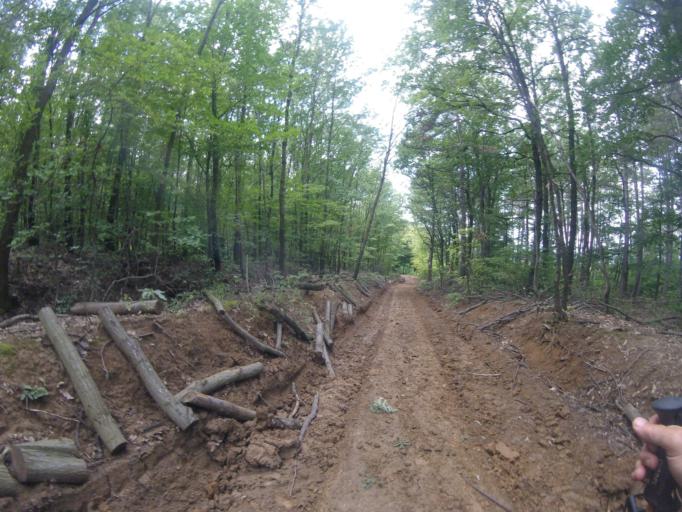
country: SK
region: Nitriansky
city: Sahy
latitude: 48.0233
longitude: 18.9668
